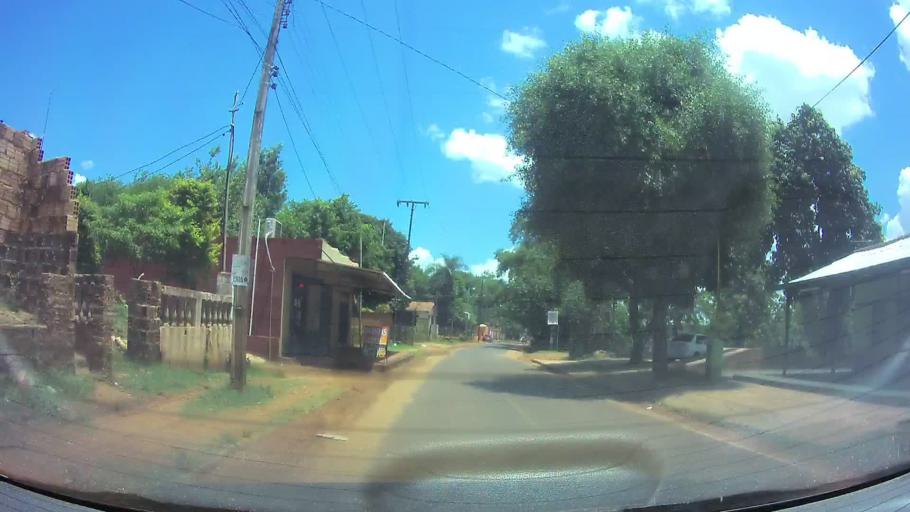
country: PY
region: Central
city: Itaugua
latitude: -25.3850
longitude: -57.3655
